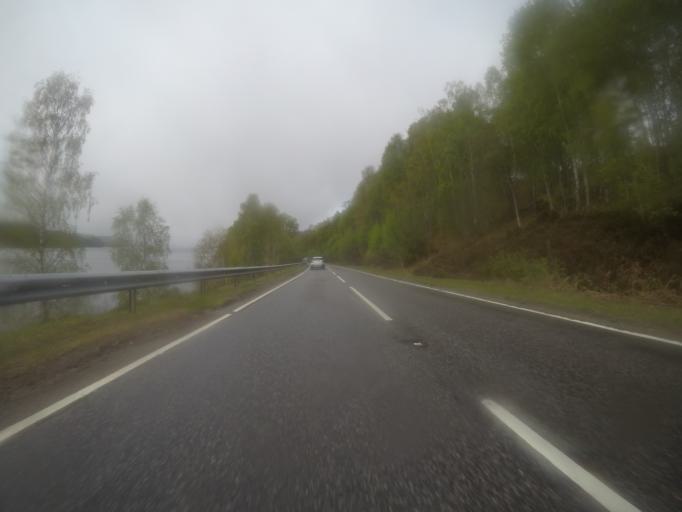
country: GB
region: Scotland
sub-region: Highland
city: Spean Bridge
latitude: 57.0816
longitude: -4.8837
